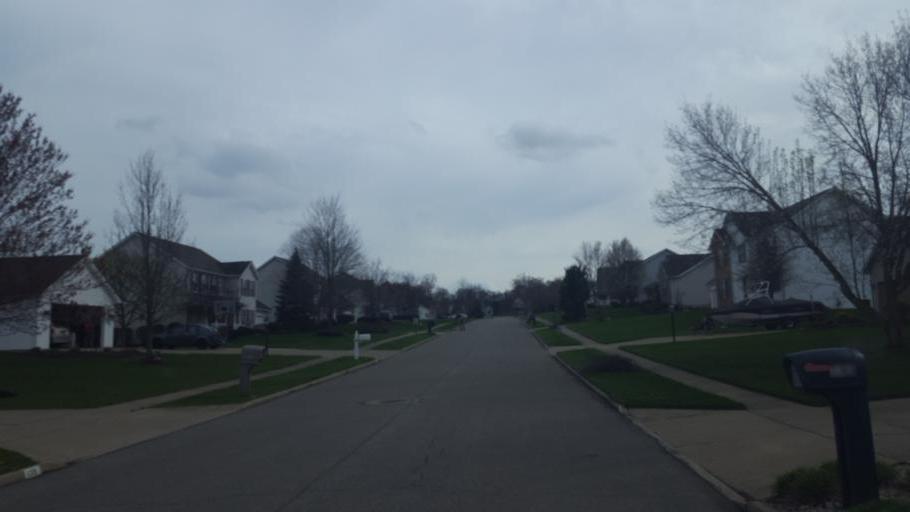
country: US
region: Ohio
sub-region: Richland County
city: Lexington
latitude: 40.6771
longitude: -82.6038
